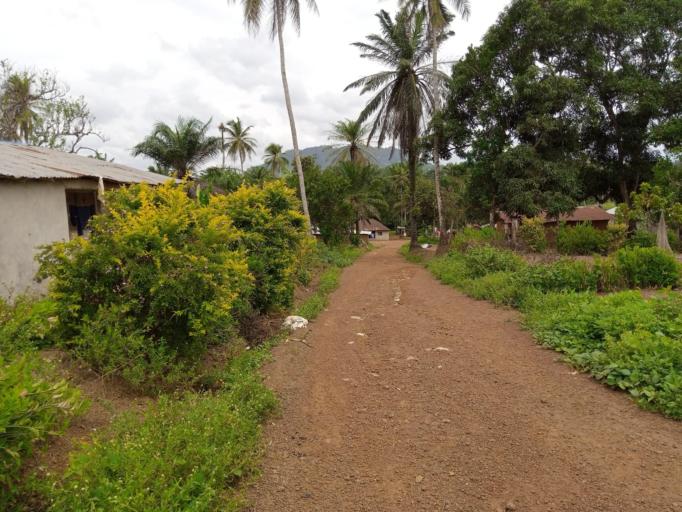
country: SL
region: Southern Province
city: Moyamba
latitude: 8.1602
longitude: -12.4254
